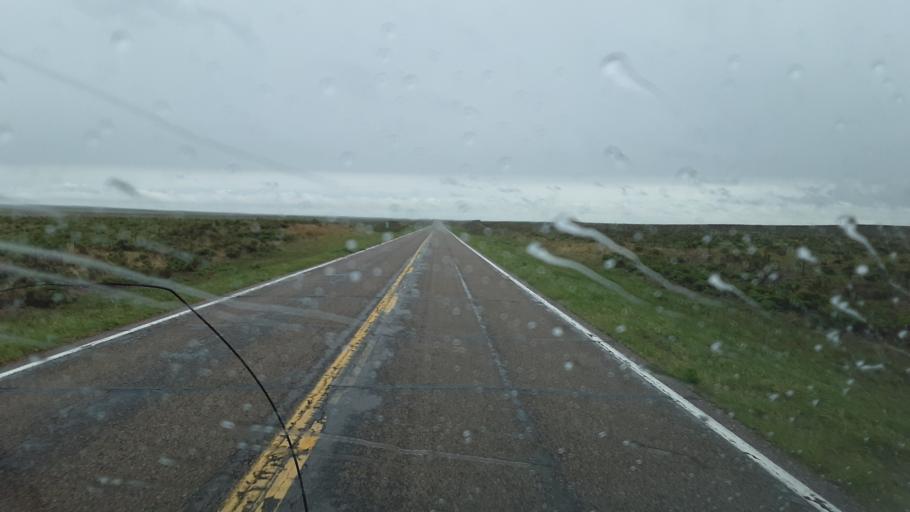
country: US
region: Colorado
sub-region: Lincoln County
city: Hugo
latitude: 38.8496
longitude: -103.1739
